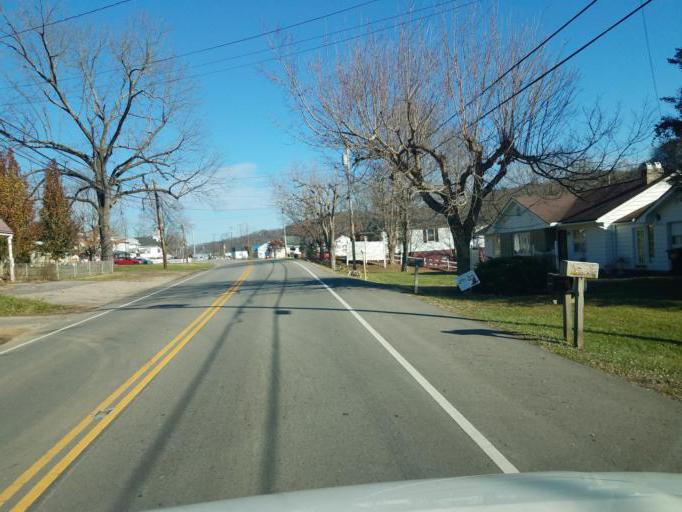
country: US
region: Ohio
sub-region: Scioto County
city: Rosemount
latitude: 38.8259
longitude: -82.9288
